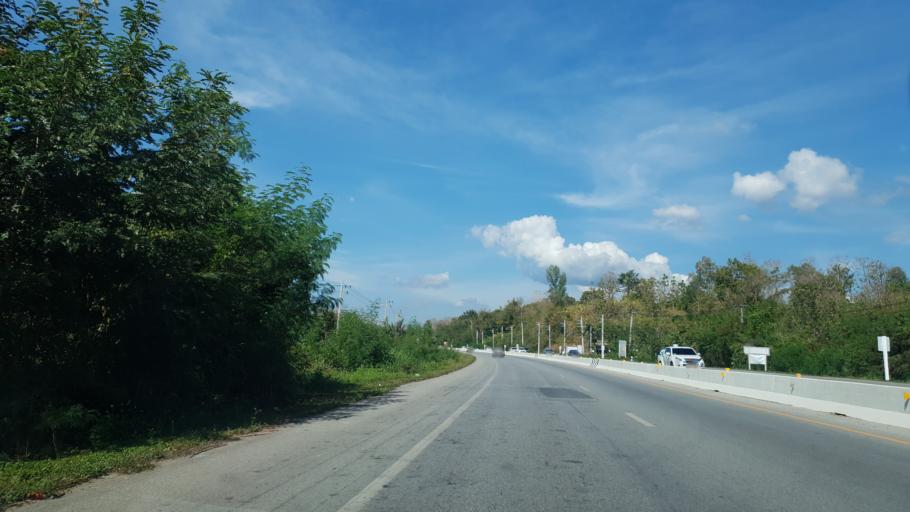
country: TH
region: Uttaradit
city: Uttaradit
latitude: 17.7192
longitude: 100.1354
